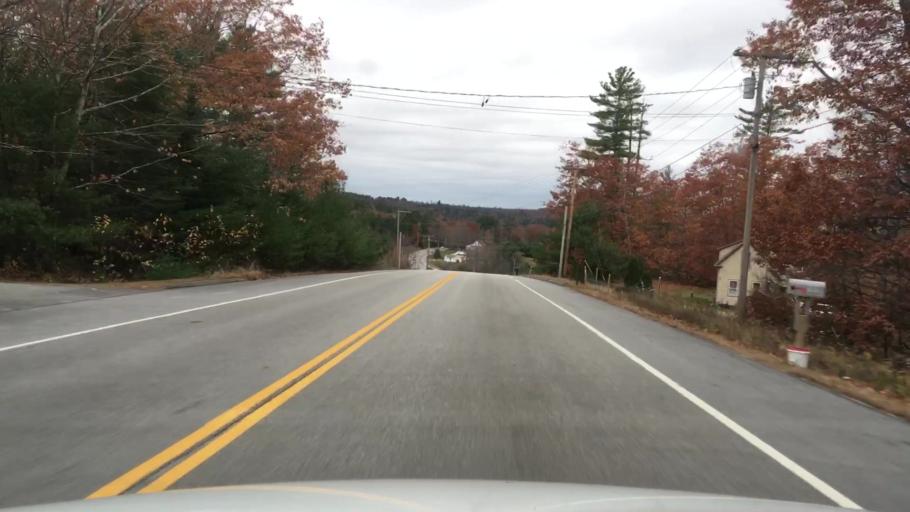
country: US
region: Maine
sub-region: Hancock County
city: Orland
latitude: 44.5578
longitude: -68.6999
